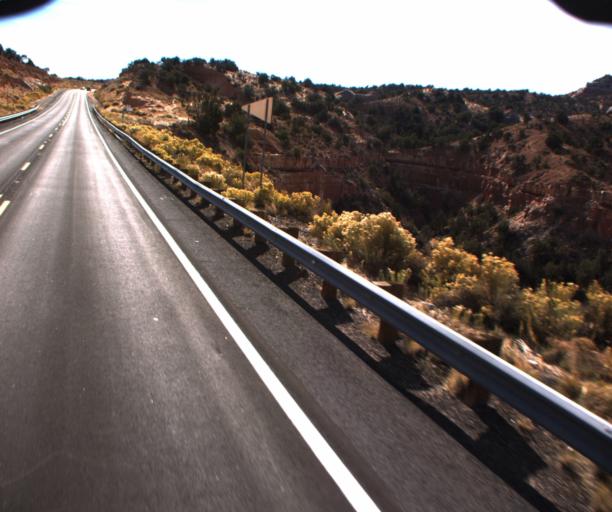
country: US
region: Arizona
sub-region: Coconino County
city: Kaibito
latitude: 36.6027
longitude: -110.9175
